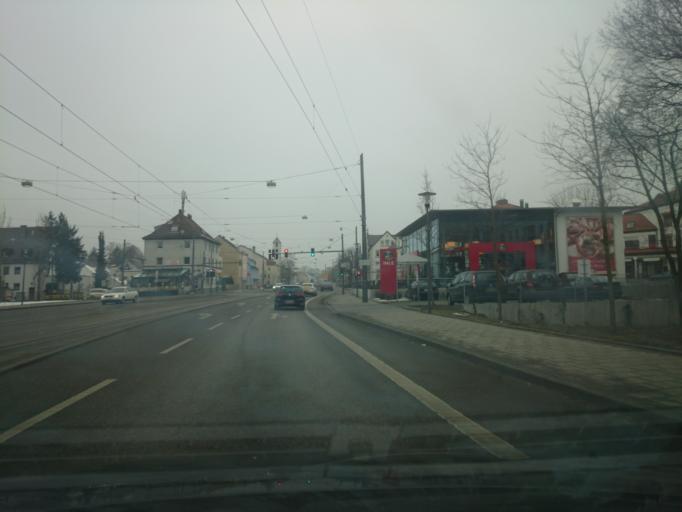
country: DE
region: Bavaria
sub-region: Swabia
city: Friedberg
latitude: 48.3554
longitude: 10.9499
